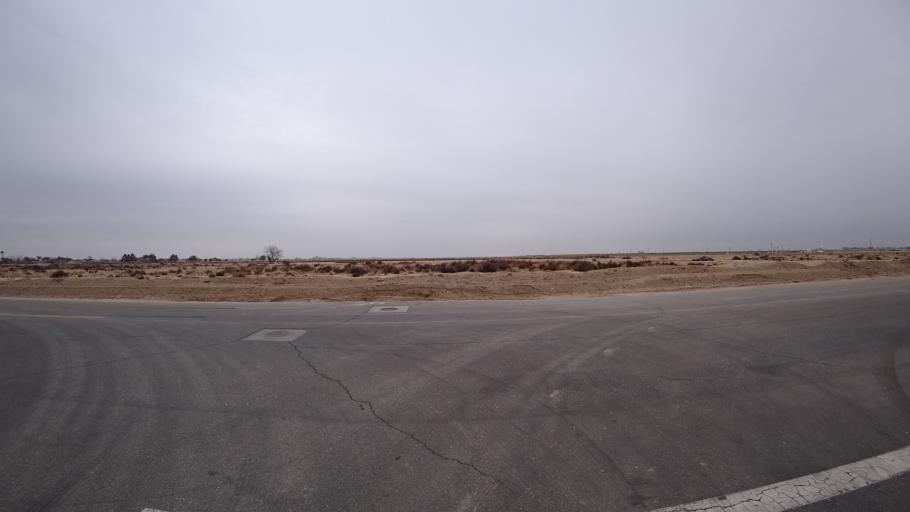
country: US
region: California
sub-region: Kern County
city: Bakersfield
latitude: 35.3471
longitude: -118.9532
